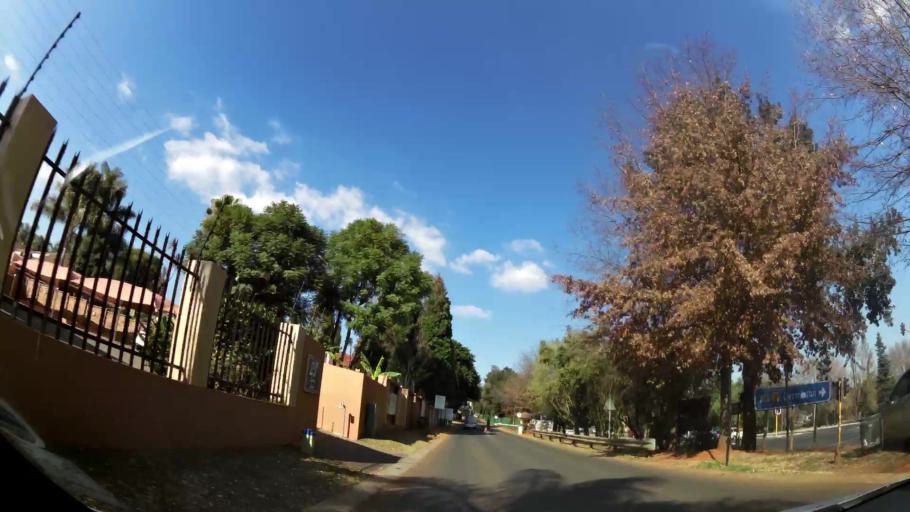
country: ZA
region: Gauteng
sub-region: Ekurhuleni Metropolitan Municipality
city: Germiston
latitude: -26.1891
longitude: 28.1358
